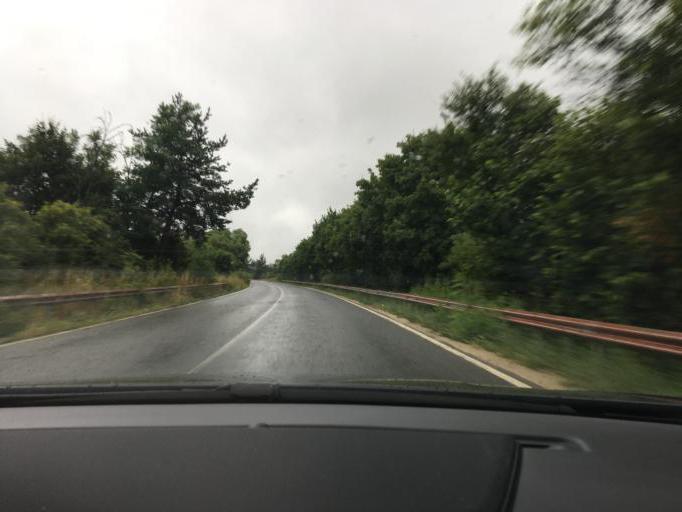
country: MK
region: Kriva Palanka
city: Kriva Palanka
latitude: 42.2302
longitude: 22.4868
